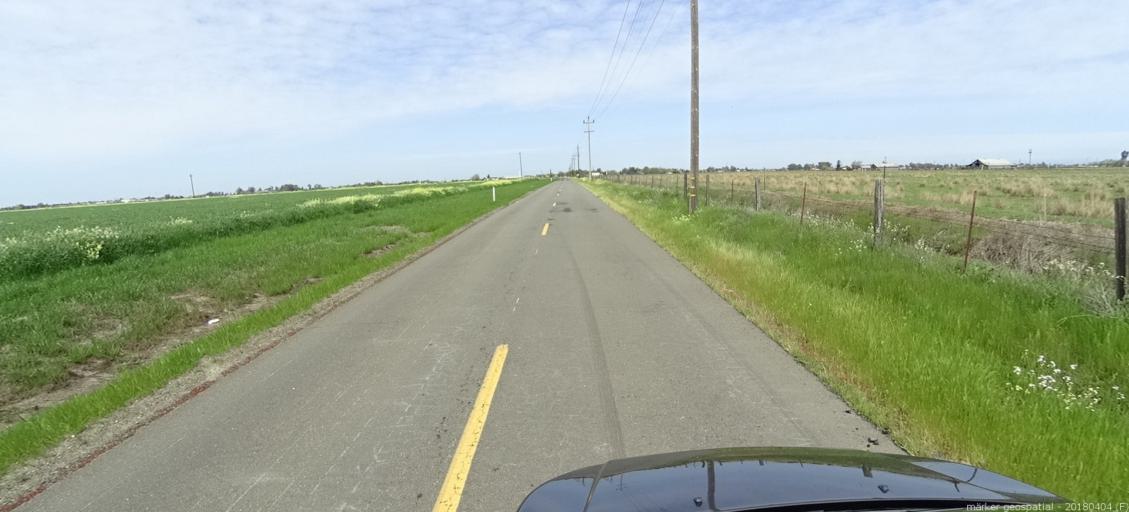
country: US
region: California
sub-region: Sacramento County
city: Herald
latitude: 38.2718
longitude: -121.2642
